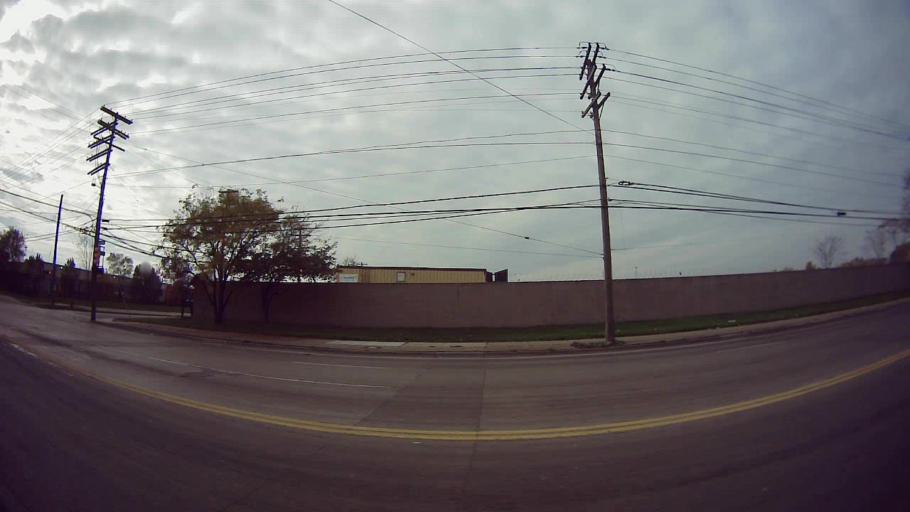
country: US
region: Michigan
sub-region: Wayne County
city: Hamtramck
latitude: 42.3665
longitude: -83.0537
